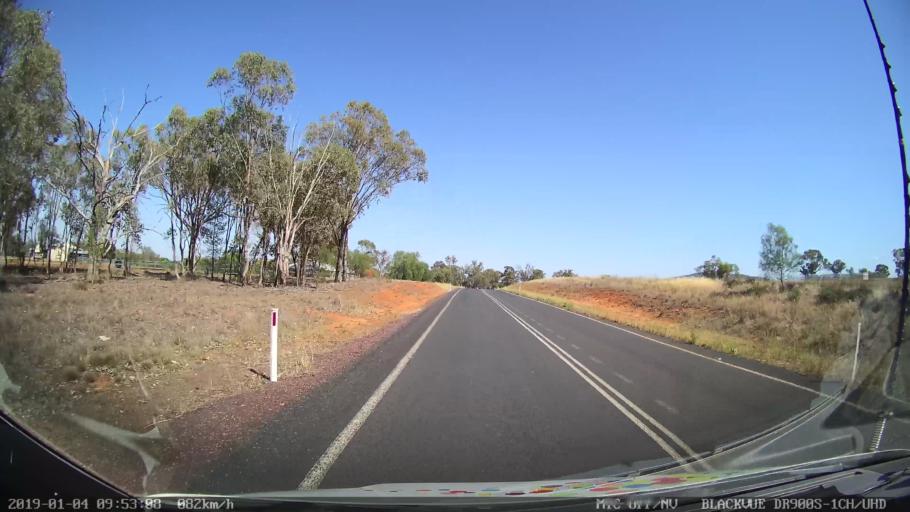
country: AU
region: New South Wales
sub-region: Cabonne
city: Canowindra
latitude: -33.5559
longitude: 148.4225
